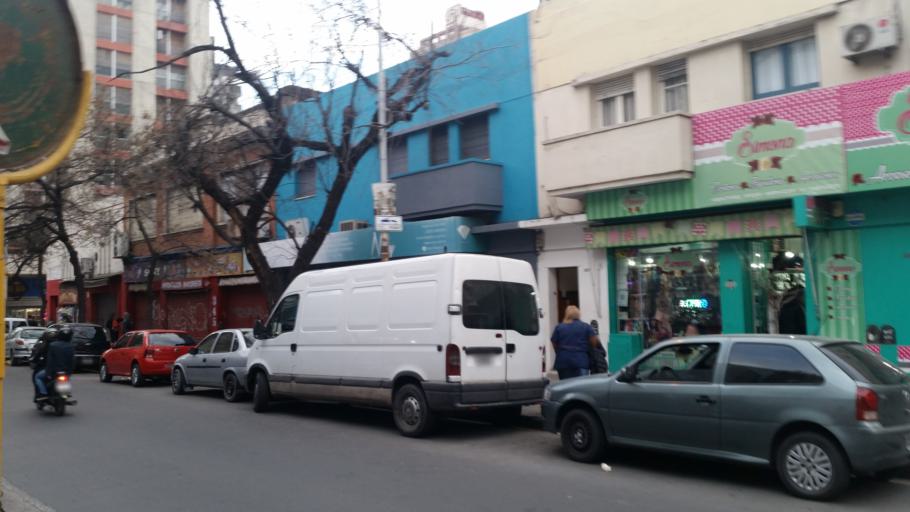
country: AR
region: Cordoba
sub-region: Departamento de Capital
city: Cordoba
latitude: -31.4207
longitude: -64.1844
